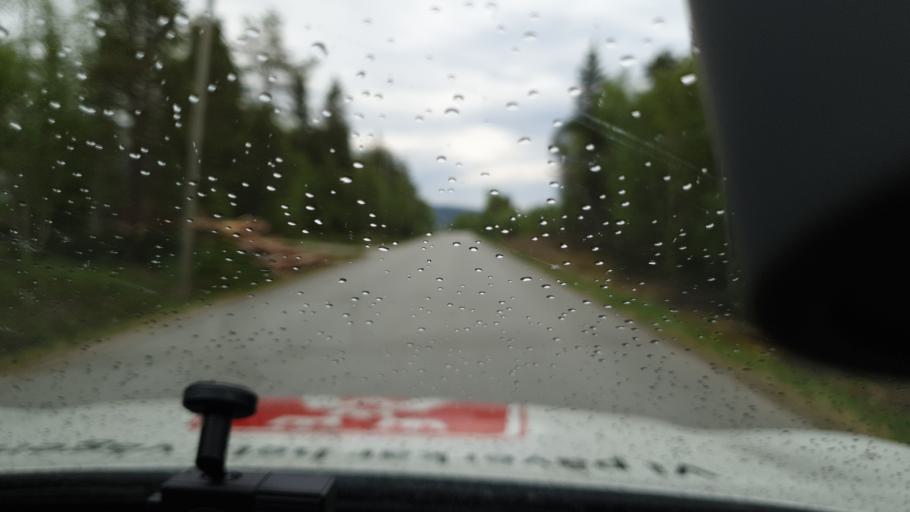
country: SE
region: Vaesterbotten
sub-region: Storumans Kommun
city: Fristad
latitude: 65.9572
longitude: 16.1961
